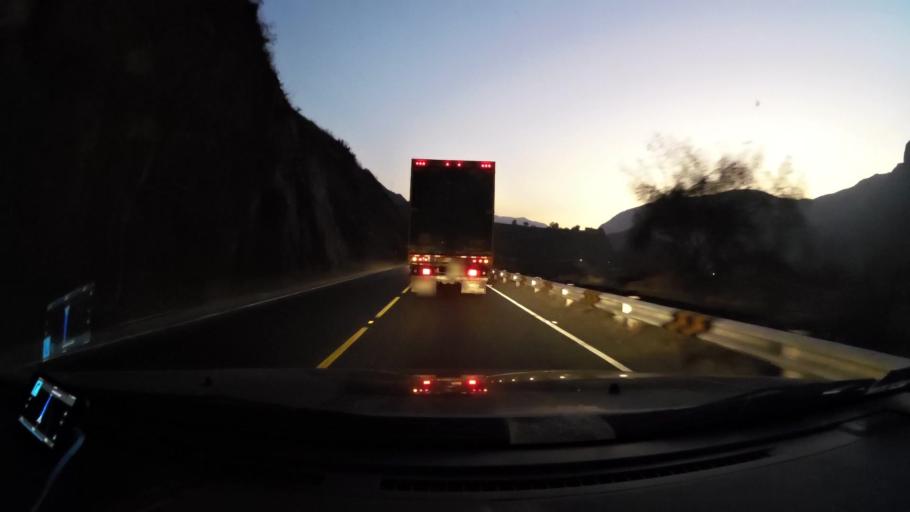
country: PE
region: Lima
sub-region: Provincia de Huarochiri
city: Cocachacra
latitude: -11.9053
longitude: -76.5197
